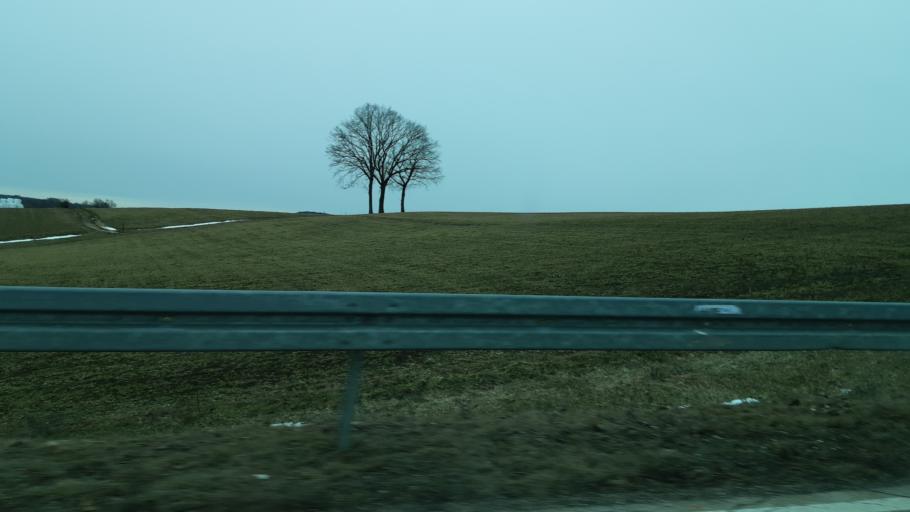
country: PL
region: Podlasie
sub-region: Suwalki
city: Suwalki
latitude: 54.3284
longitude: 22.9618
